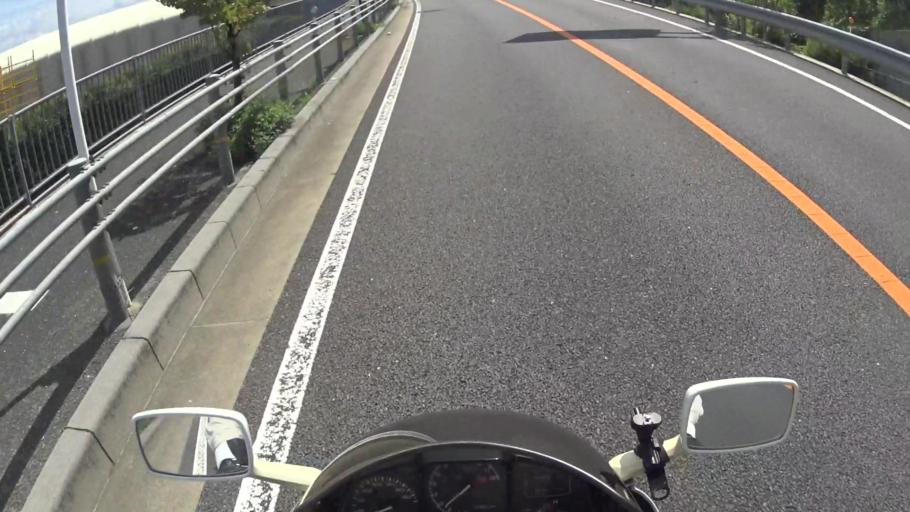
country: JP
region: Kyoto
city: Yawata
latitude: 34.9025
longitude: 135.6978
